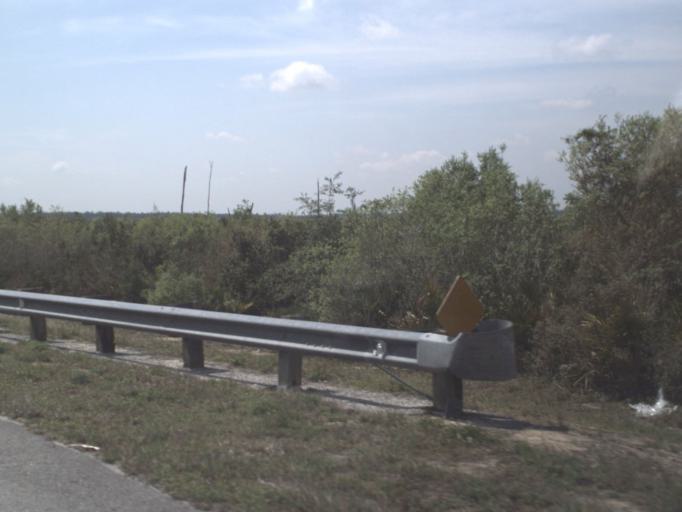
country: US
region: Florida
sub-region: Lake County
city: Astor
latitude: 29.2403
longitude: -81.6471
